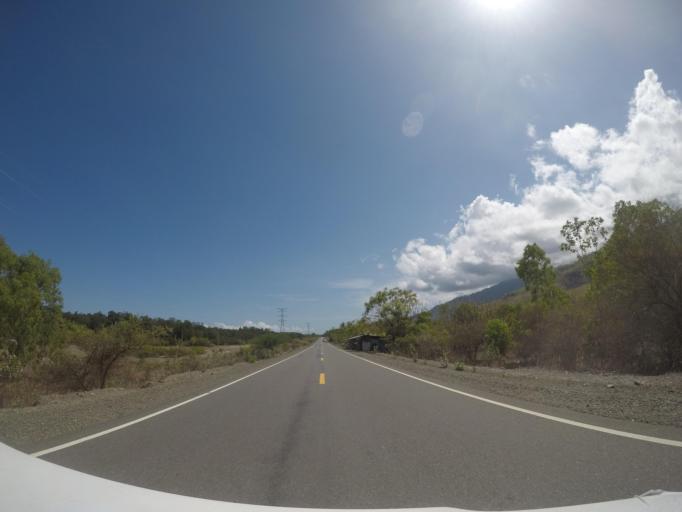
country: ID
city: Metinaro
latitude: -8.5064
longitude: 125.8076
